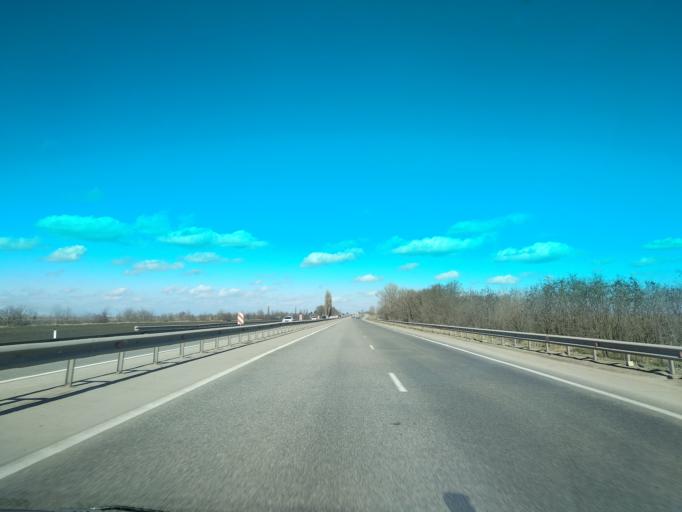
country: RU
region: Krasnodarskiy
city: Agronom
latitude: 45.1441
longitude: 39.1095
